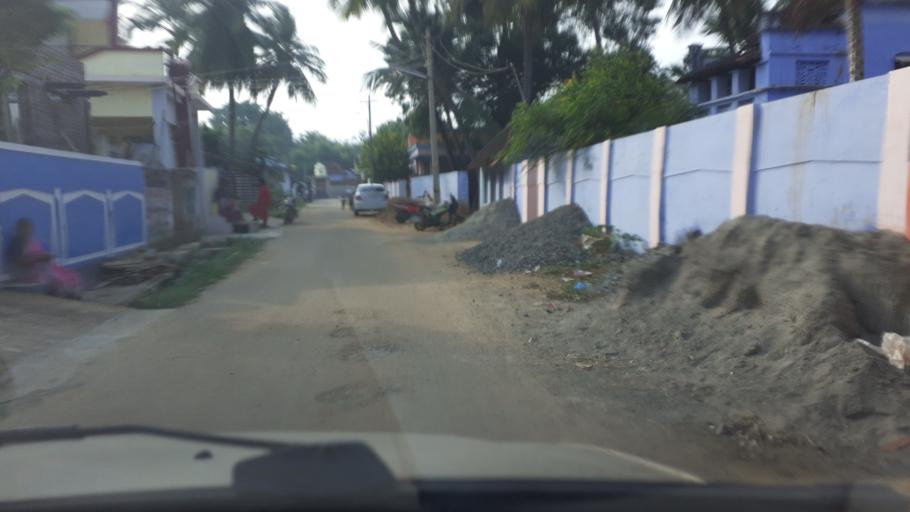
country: IN
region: Tamil Nadu
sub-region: Tirunelveli Kattabo
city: Kalakkadu
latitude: 8.4742
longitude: 77.5950
